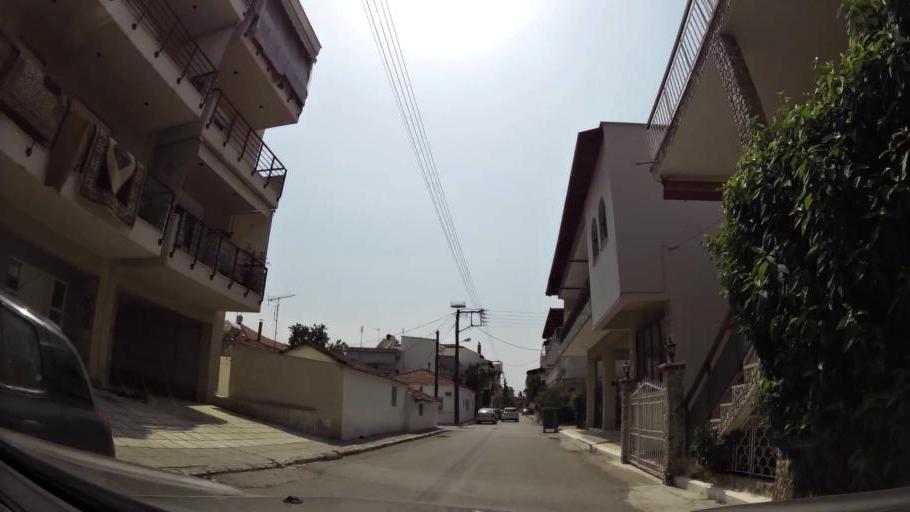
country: GR
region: Central Macedonia
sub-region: Nomos Thessalonikis
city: Nea Magnisia
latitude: 40.6871
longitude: 22.8476
